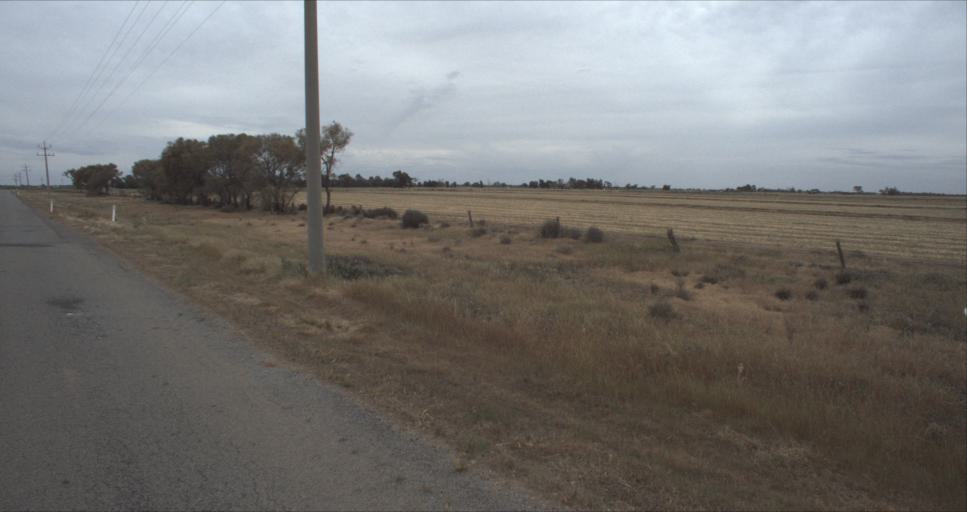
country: AU
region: New South Wales
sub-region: Leeton
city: Leeton
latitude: -34.4957
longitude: 146.4006
